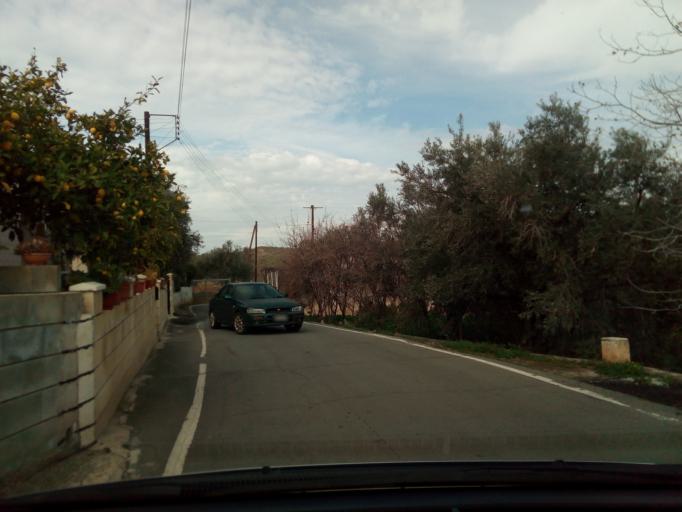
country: CY
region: Lefkosia
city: Astromeritis
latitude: 35.0755
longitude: 32.9950
